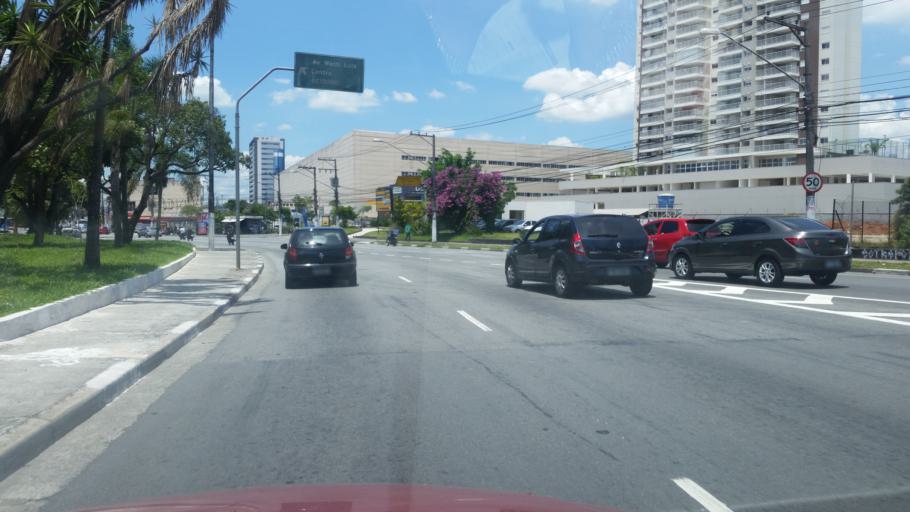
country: BR
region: Sao Paulo
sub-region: Diadema
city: Diadema
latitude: -23.6608
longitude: -46.7052
